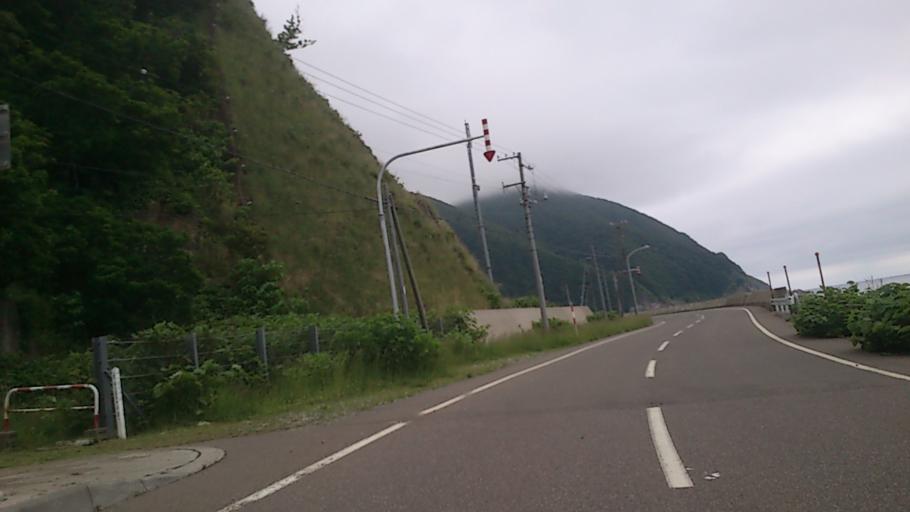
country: JP
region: Hokkaido
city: Kamiiso
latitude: 42.2777
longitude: 139.7852
